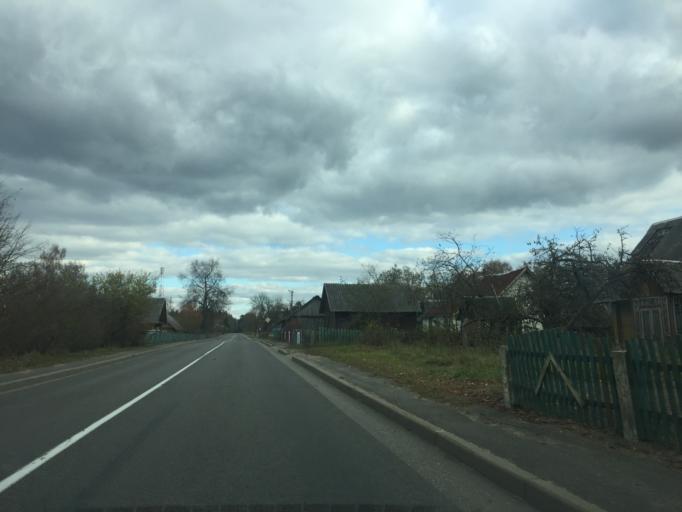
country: BY
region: Minsk
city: Svir
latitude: 54.9179
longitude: 26.4560
